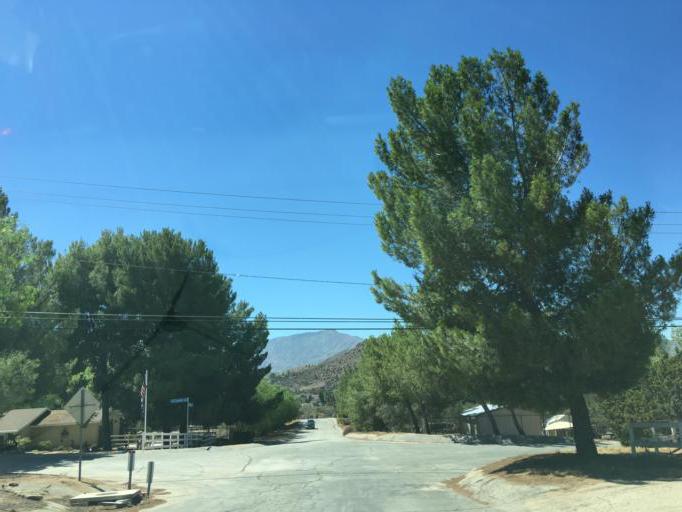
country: US
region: California
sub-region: Los Angeles County
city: Acton
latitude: 34.4738
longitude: -118.1827
